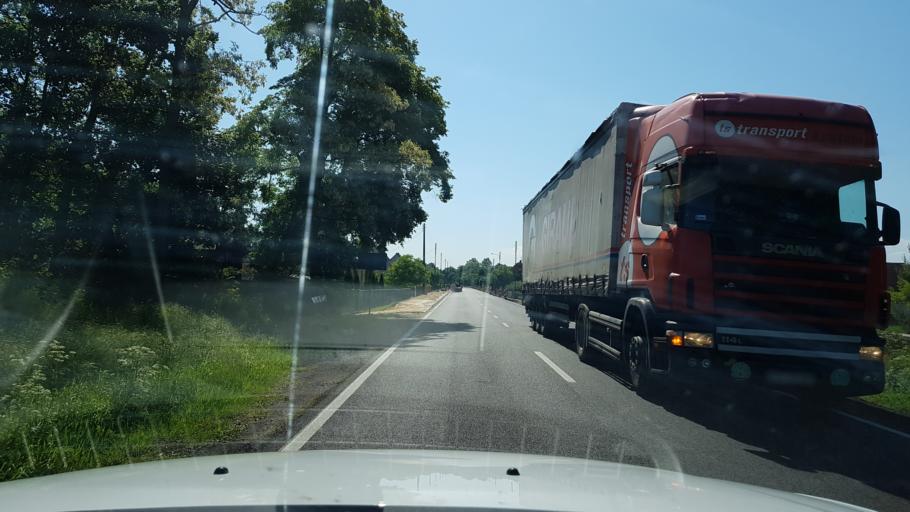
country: PL
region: West Pomeranian Voivodeship
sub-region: Powiat mysliborski
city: Boleszkowice
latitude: 52.6905
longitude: 14.6284
